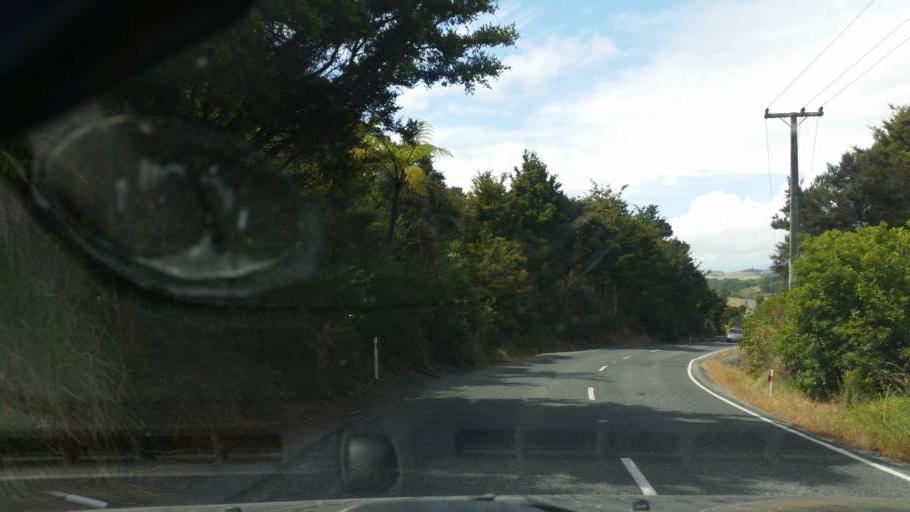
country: NZ
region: Auckland
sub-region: Auckland
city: Wellsford
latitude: -36.1146
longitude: 174.5429
